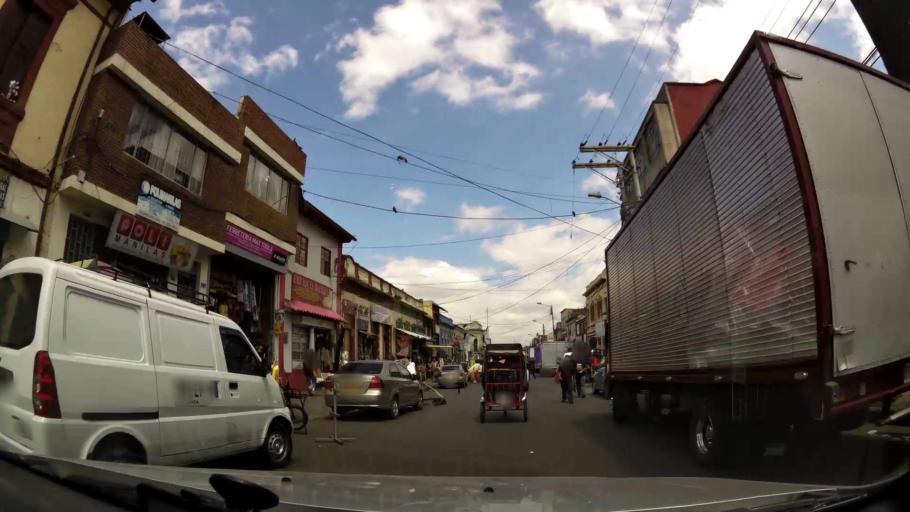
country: CO
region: Bogota D.C.
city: Bogota
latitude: 4.6035
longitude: -74.0831
